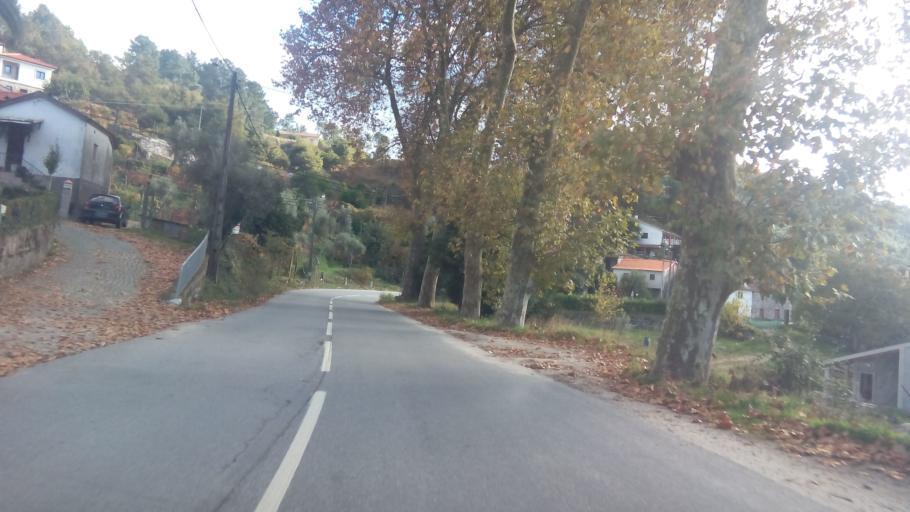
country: PT
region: Porto
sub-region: Amarante
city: Amarante
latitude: 41.2651
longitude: -8.0126
